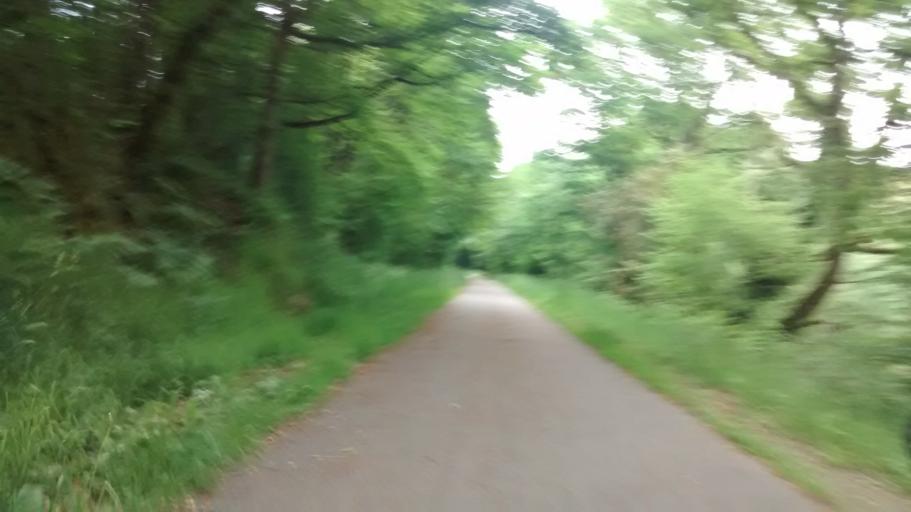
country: FR
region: Brittany
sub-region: Departement du Morbihan
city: Molac
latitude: 47.7238
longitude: -2.4214
